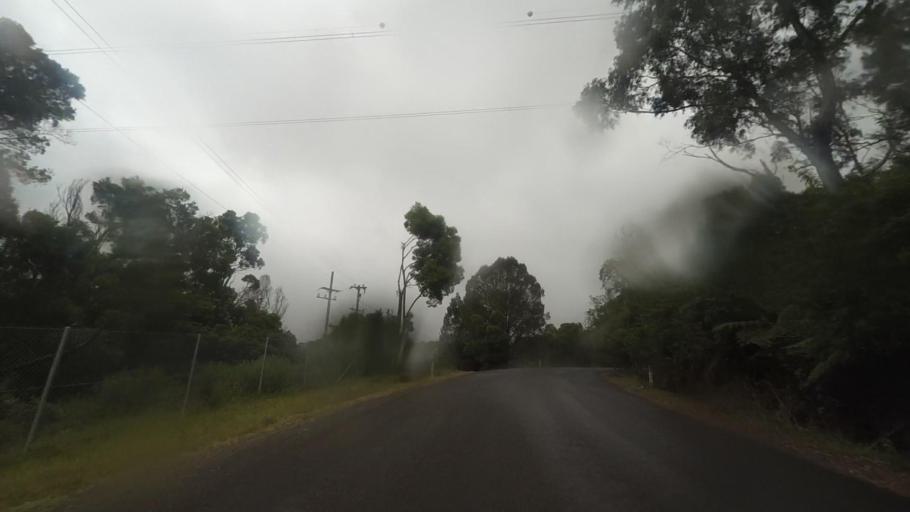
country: AU
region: New South Wales
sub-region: Wollongong
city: Cordeaux Heights
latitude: -34.4117
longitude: 150.8148
